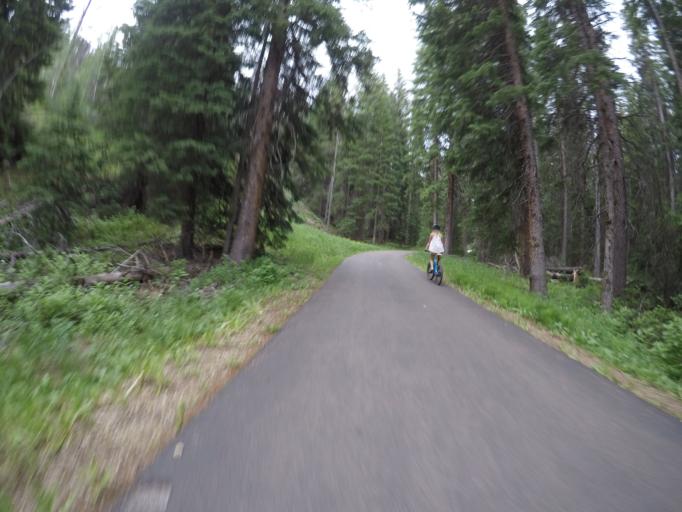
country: US
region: Colorado
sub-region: Grand County
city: Fraser
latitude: 39.9011
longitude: -105.7764
